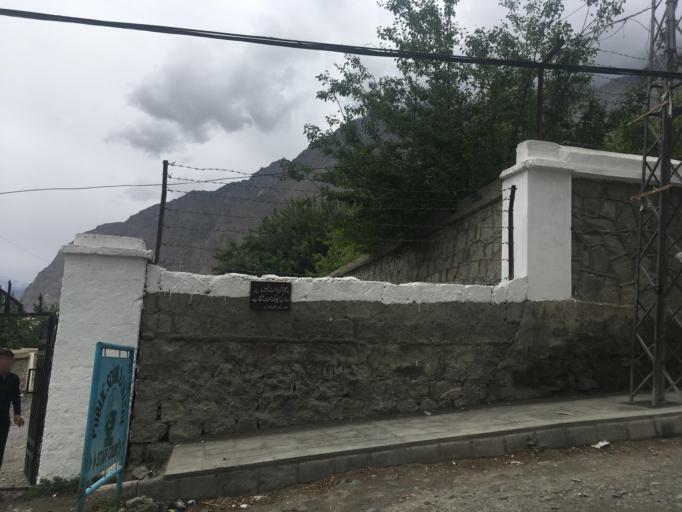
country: PK
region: Gilgit-Baltistan
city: Skardu
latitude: 35.2745
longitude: 75.6363
